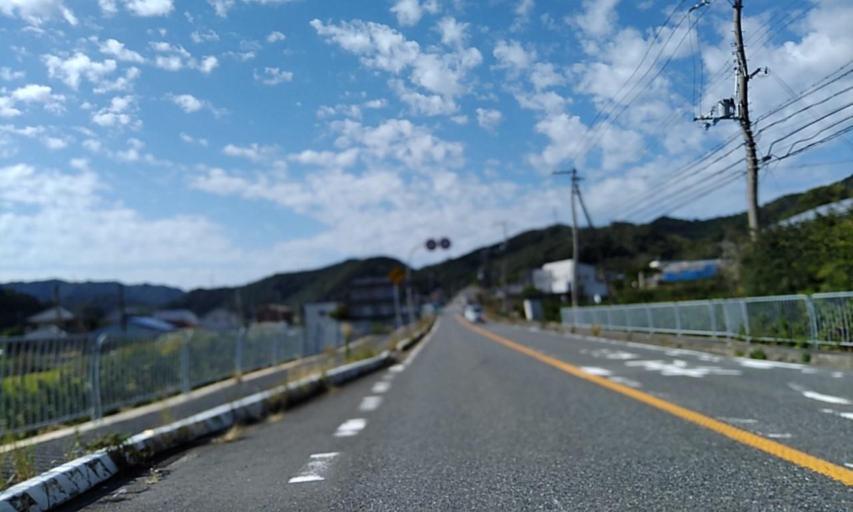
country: JP
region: Wakayama
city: Gobo
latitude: 33.9717
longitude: 135.1332
